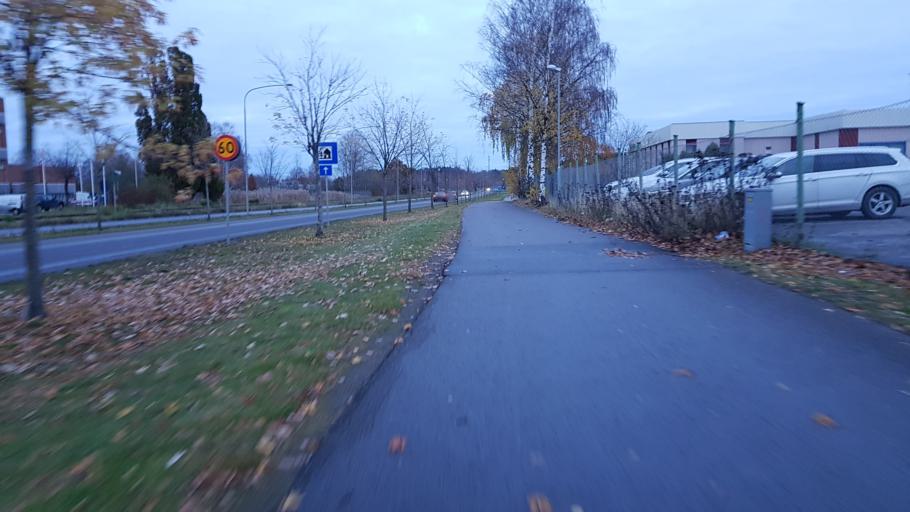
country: SE
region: OEstergoetland
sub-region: Norrkopings Kommun
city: Norrkoping
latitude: 58.5921
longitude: 16.2204
